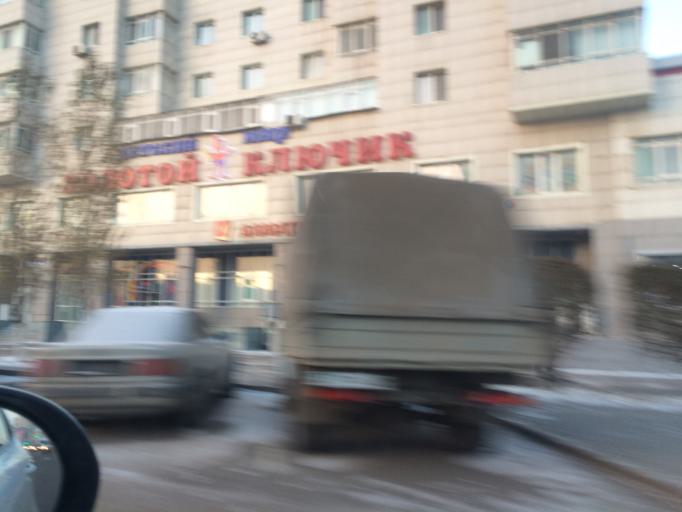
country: KZ
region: Astana Qalasy
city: Astana
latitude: 51.1858
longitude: 71.4082
